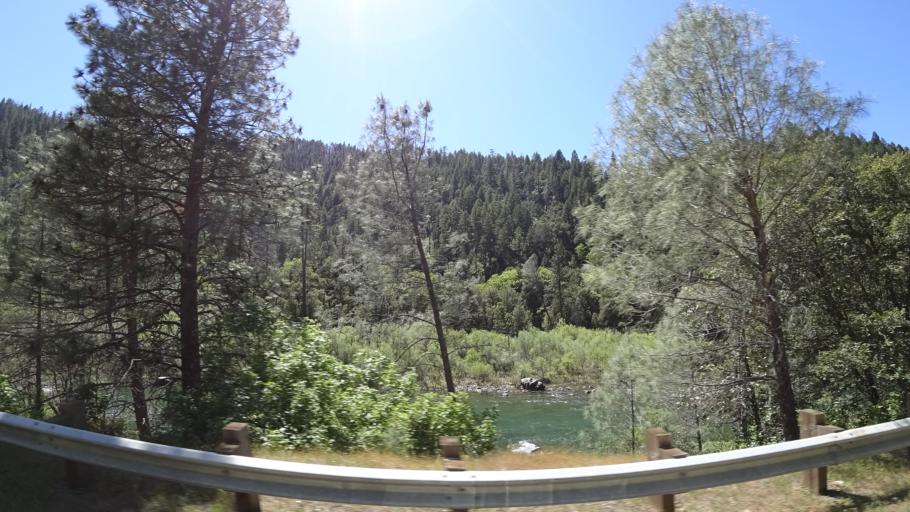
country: US
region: California
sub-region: Trinity County
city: Hayfork
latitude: 40.7637
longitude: -123.2905
